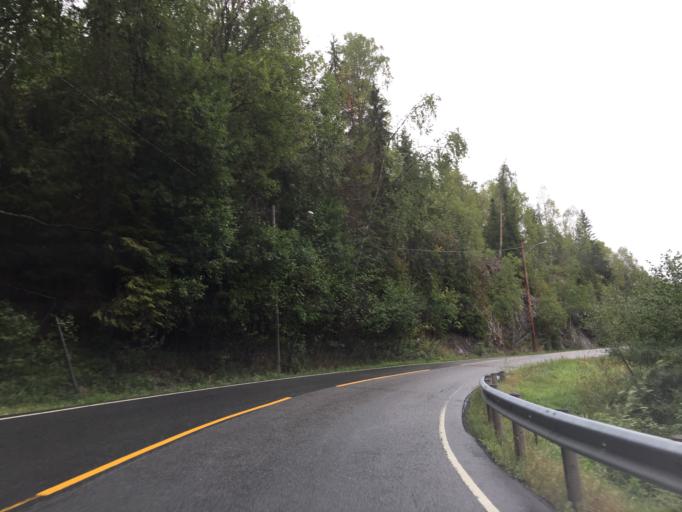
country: NO
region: Akershus
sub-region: Baerum
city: Lysaker
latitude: 60.0092
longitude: 10.6144
